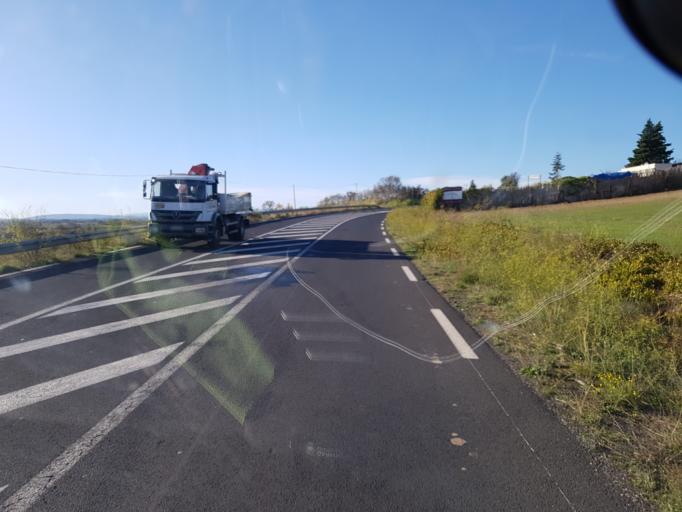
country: FR
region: Languedoc-Roussillon
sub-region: Departement de l'Aude
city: Coursan
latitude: 43.2709
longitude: 3.0792
